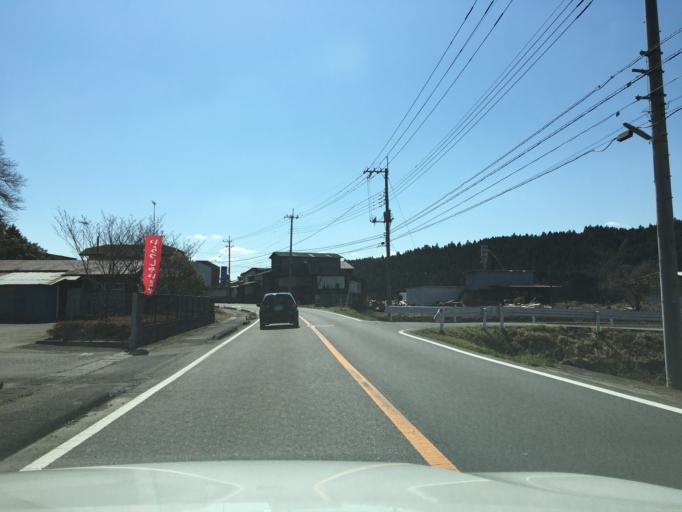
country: JP
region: Tochigi
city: Kuroiso
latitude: 36.9649
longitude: 140.1563
